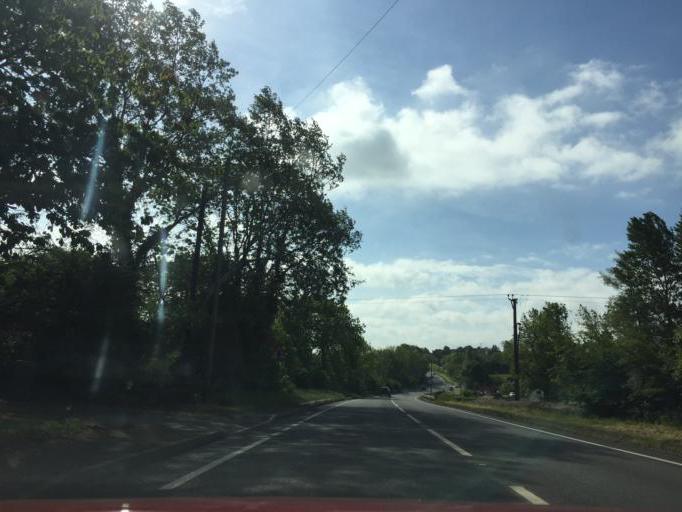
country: GB
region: England
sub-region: Northamptonshire
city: Towcester
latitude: 52.1132
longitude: -0.9545
